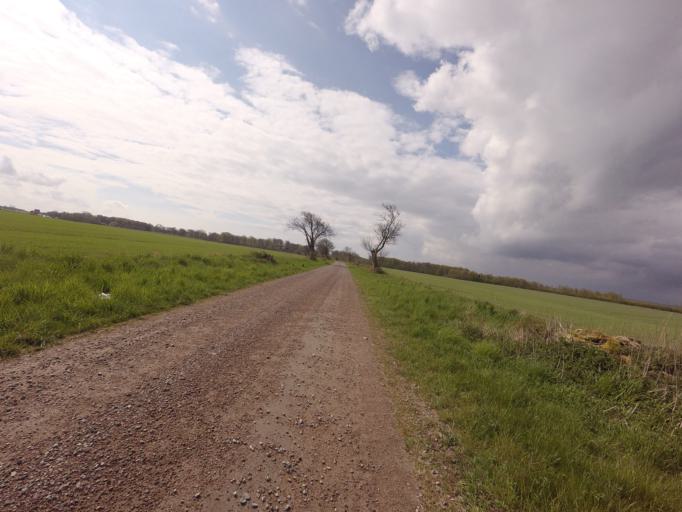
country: DK
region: Capital Region
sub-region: Helsingor Kommune
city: Helsingor
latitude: 56.1167
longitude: 12.6291
